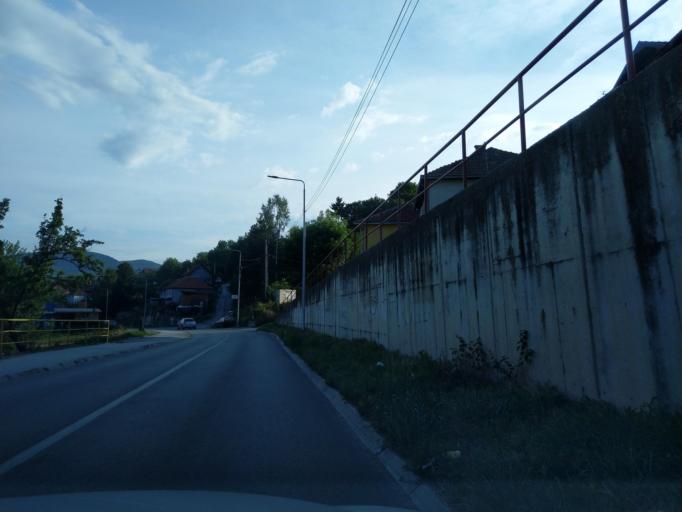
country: RS
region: Central Serbia
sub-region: Zlatiborski Okrug
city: Prijepolje
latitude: 43.3555
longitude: 19.6354
